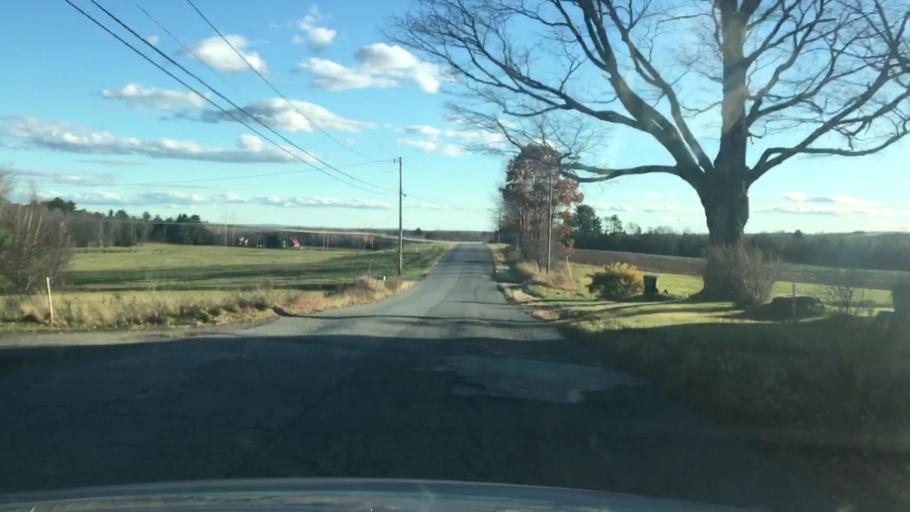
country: US
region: Maine
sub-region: Somerset County
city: Pittsfield
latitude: 44.7899
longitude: -69.4102
